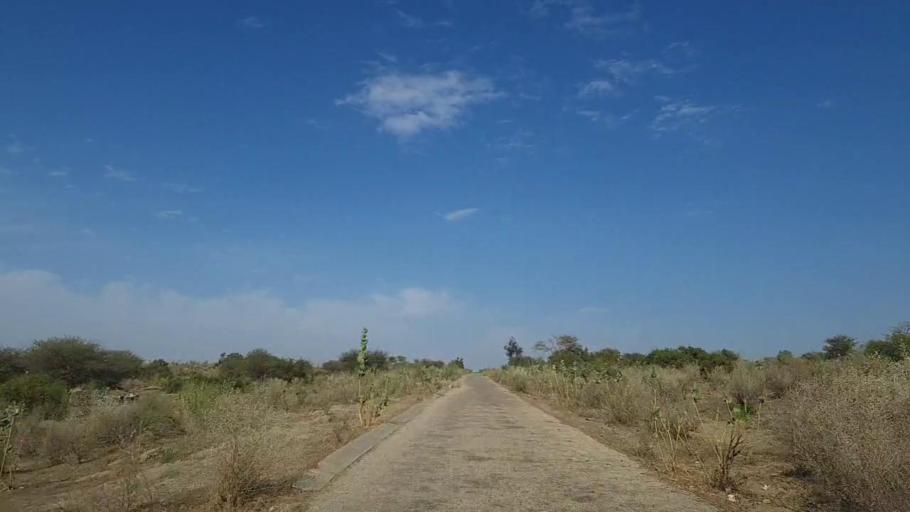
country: PK
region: Sindh
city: Naukot
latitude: 24.8471
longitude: 69.5570
